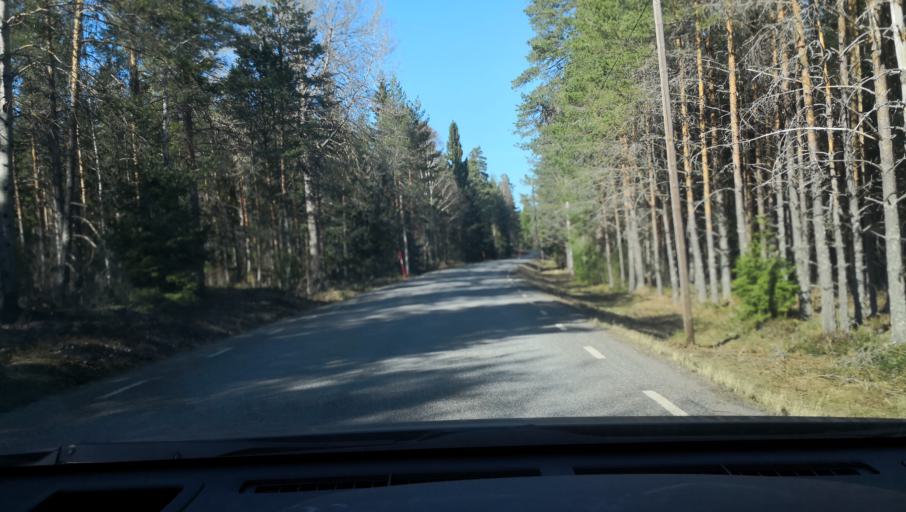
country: SE
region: Vaestmanland
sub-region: Sala Kommun
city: Sala
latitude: 60.0000
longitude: 16.4934
